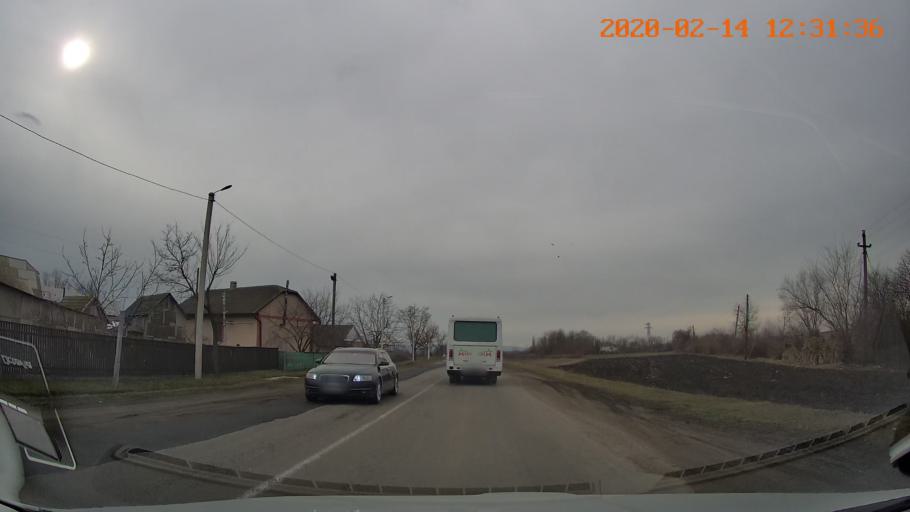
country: RO
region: Botosani
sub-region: Comuna Darabani
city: Bajura
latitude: 48.2479
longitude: 26.5560
